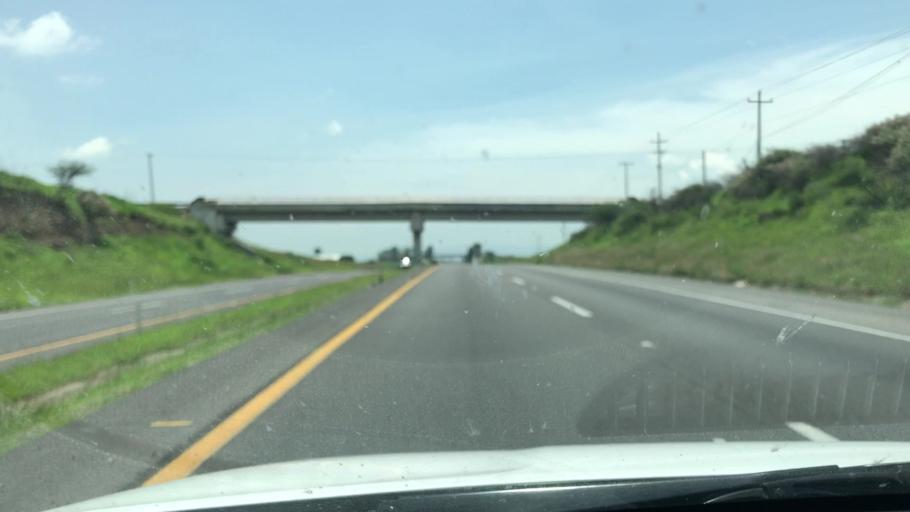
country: MX
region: Guanajuato
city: Penjamo
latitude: 20.3841
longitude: -101.7930
